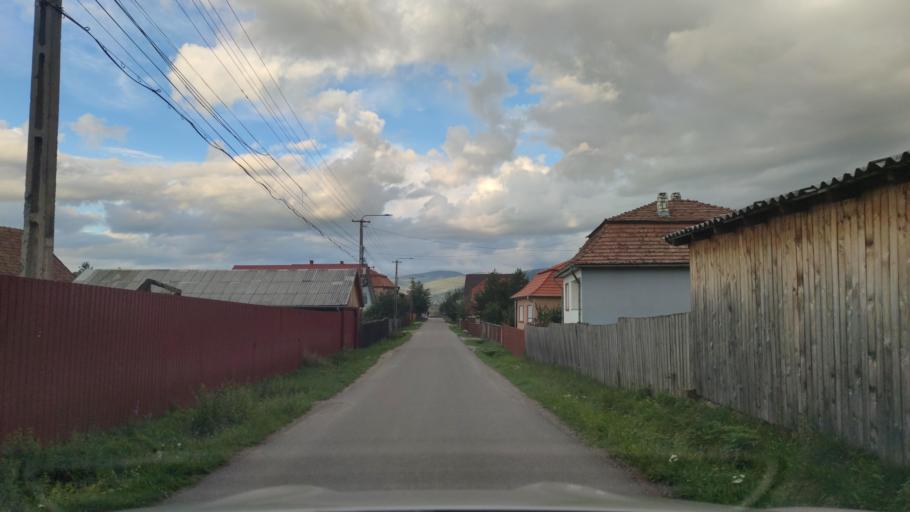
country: RO
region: Harghita
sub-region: Comuna Remetea
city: Remetea
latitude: 46.8045
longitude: 25.4553
